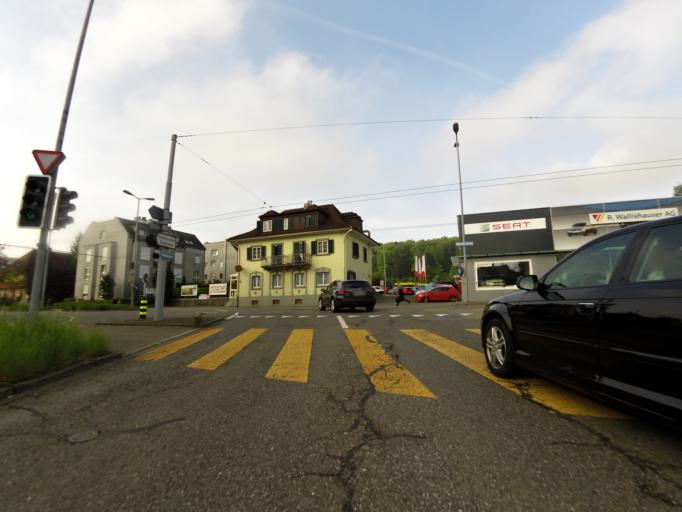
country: CH
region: Zurich
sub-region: Bezirk Zuerich
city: Zuerich (Kreis 6) / Unterstrass
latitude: 47.4040
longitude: 8.5344
